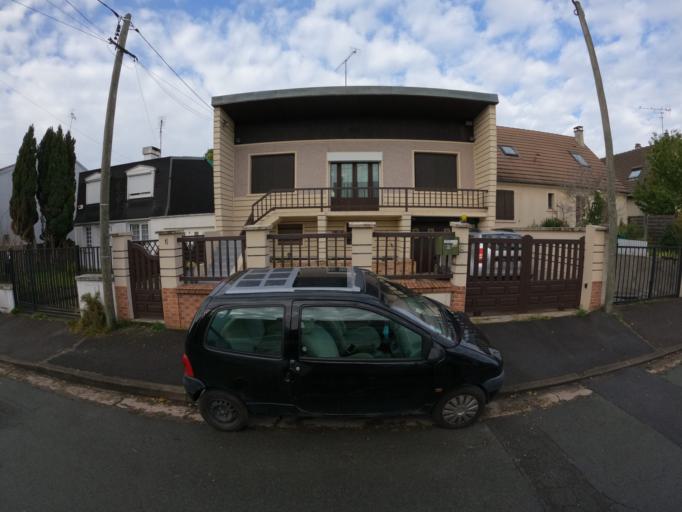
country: FR
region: Ile-de-France
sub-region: Departement de Seine-Saint-Denis
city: Coubron
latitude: 48.9077
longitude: 2.5917
